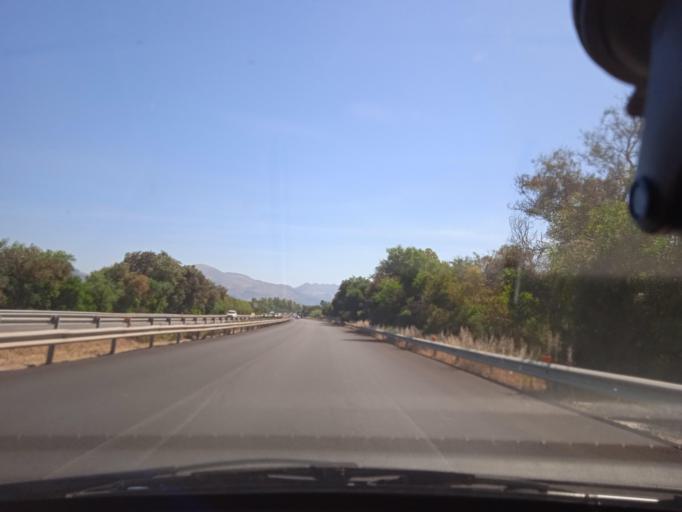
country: IT
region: Sicily
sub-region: Palermo
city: Trappeto
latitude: 38.0456
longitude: 13.0510
